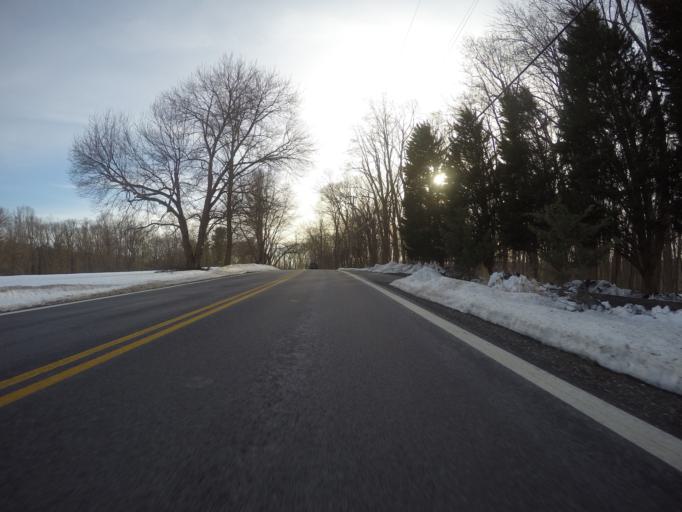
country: US
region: Maryland
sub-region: Baltimore County
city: Hampton
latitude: 39.4780
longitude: -76.5736
